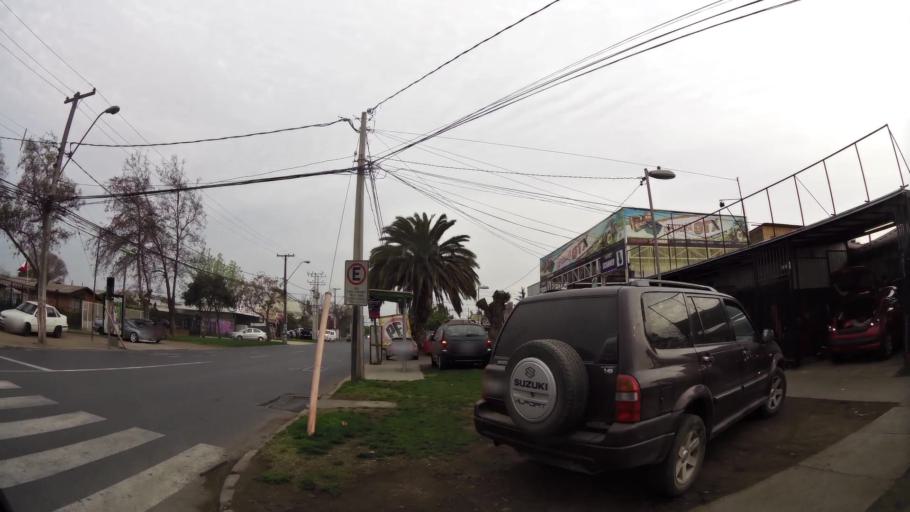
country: CL
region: Santiago Metropolitan
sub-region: Provincia de Santiago
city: Lo Prado
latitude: -33.5154
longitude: -70.7755
